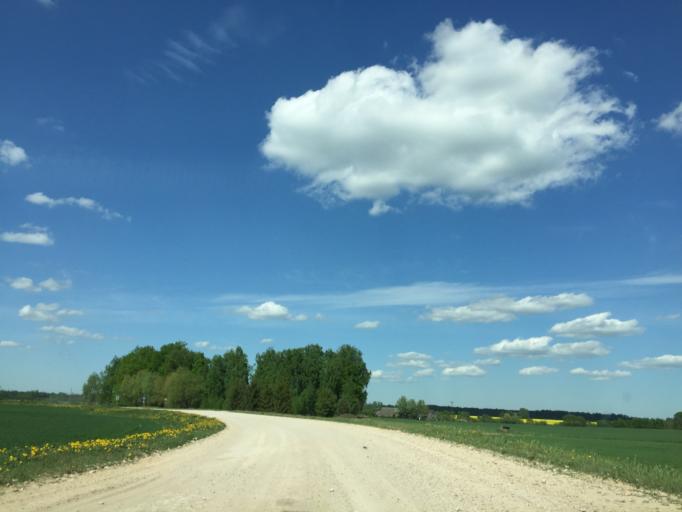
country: LV
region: Rundales
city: Pilsrundale
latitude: 56.3769
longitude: 24.0793
